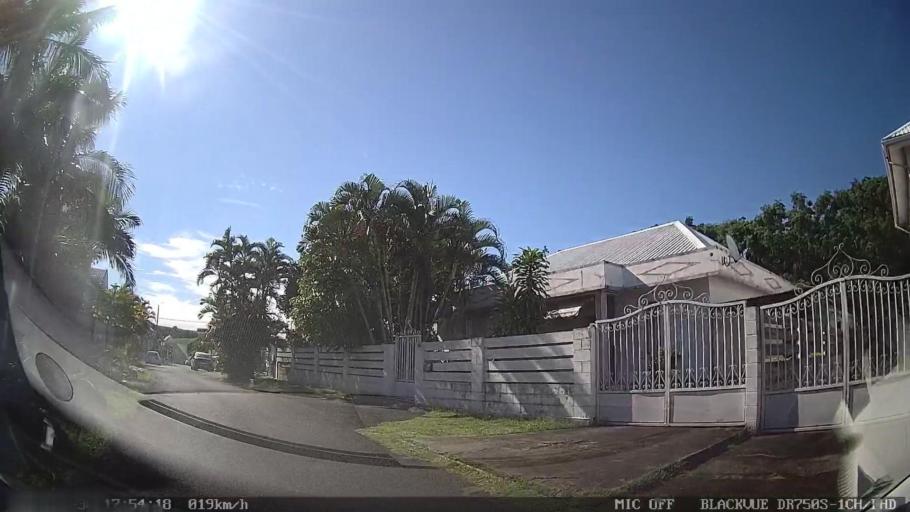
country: RE
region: Reunion
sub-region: Reunion
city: Sainte-Marie
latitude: -20.9079
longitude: 55.5207
